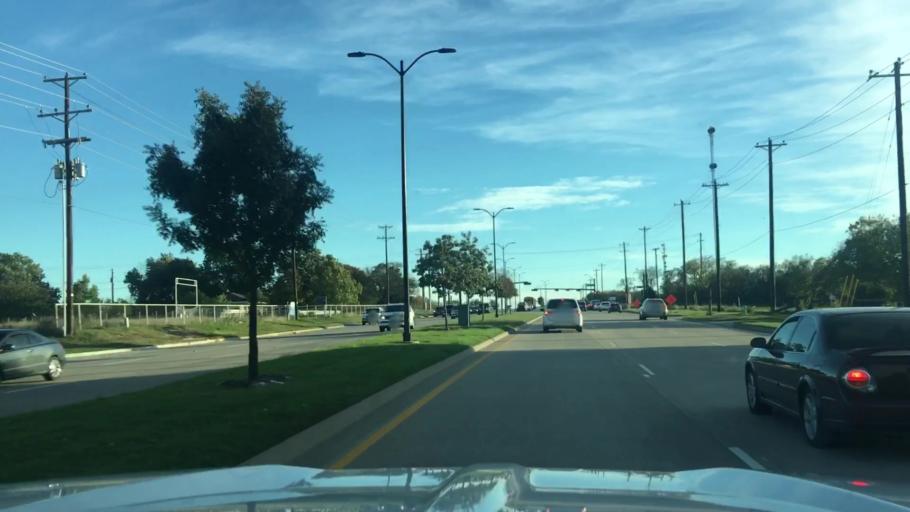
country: US
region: Texas
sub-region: Collin County
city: Prosper
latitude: 33.2064
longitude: -96.8028
